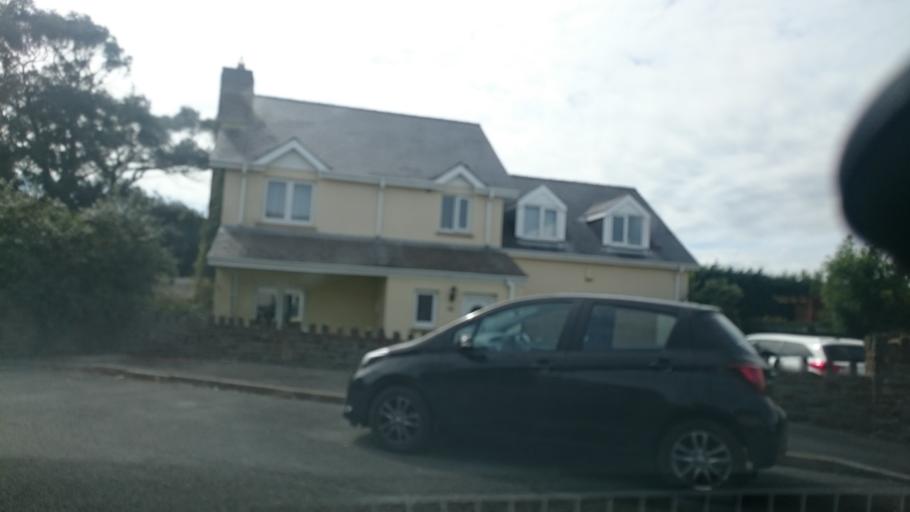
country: GB
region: Wales
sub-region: Pembrokeshire
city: Haverfordwest
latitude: 51.7851
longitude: -4.9705
